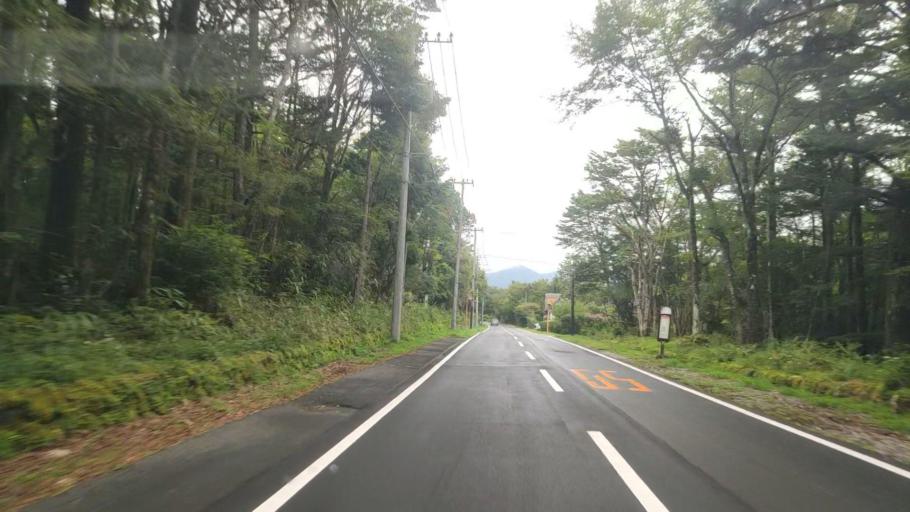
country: JP
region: Shizuoka
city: Gotemba
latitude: 35.2674
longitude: 138.8040
